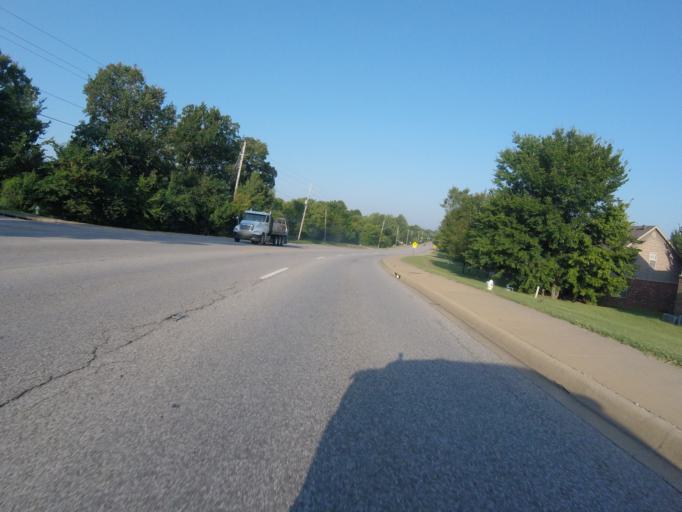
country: US
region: Arkansas
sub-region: Washington County
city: Fayetteville
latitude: 36.0780
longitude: -94.1851
